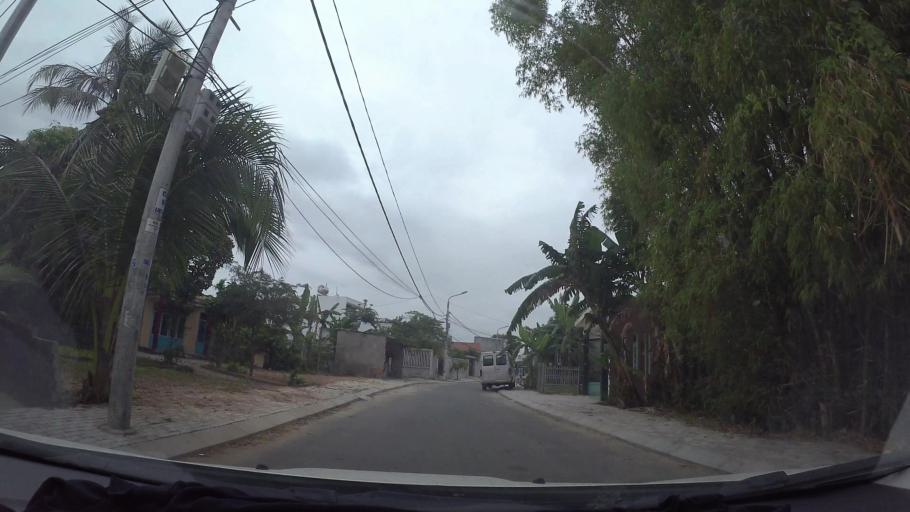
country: VN
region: Da Nang
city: Lien Chieu
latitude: 16.1059
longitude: 108.1295
